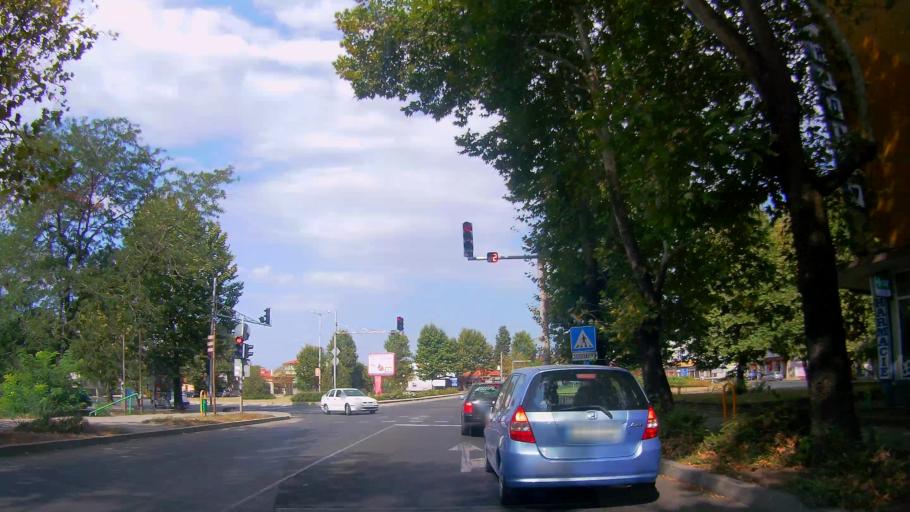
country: BG
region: Burgas
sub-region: Obshtina Aytos
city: Aytos
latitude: 42.6987
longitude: 27.2498
